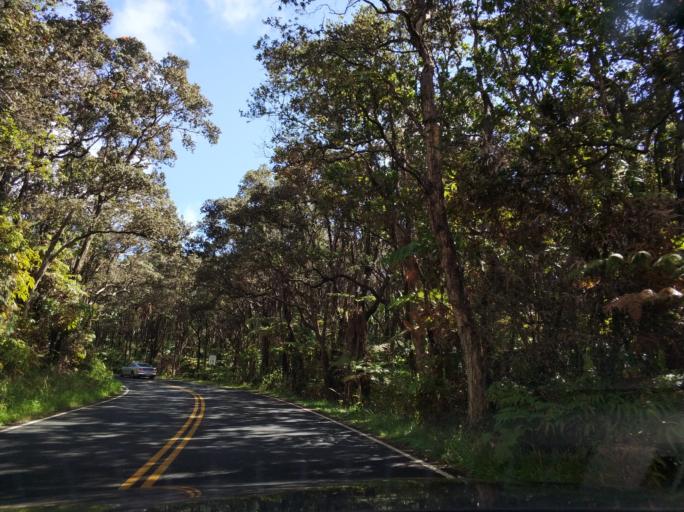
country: US
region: Hawaii
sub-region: Hawaii County
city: Volcano
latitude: 19.4148
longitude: -155.2407
